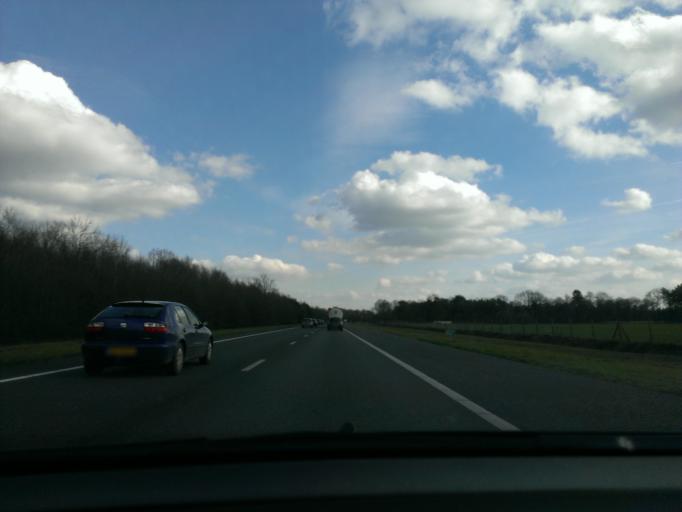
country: NL
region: Overijssel
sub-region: Gemeente Borne
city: Borne
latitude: 52.2861
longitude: 6.7394
